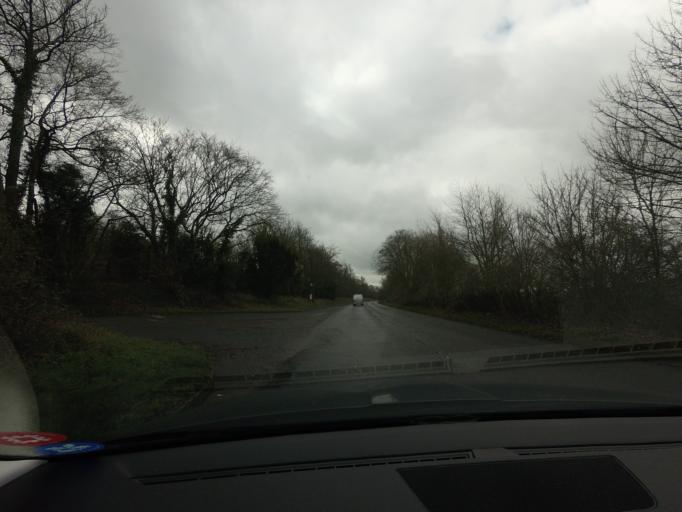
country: GB
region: England
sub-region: Kent
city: Eynsford
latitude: 51.3559
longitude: 0.2005
